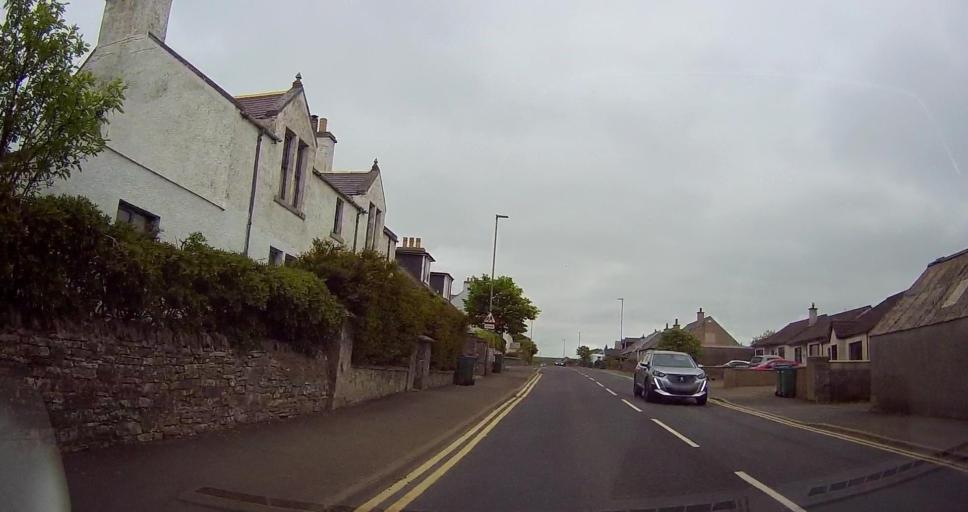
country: GB
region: Scotland
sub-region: Orkney Islands
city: Kirkwall
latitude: 58.9757
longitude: -2.9534
